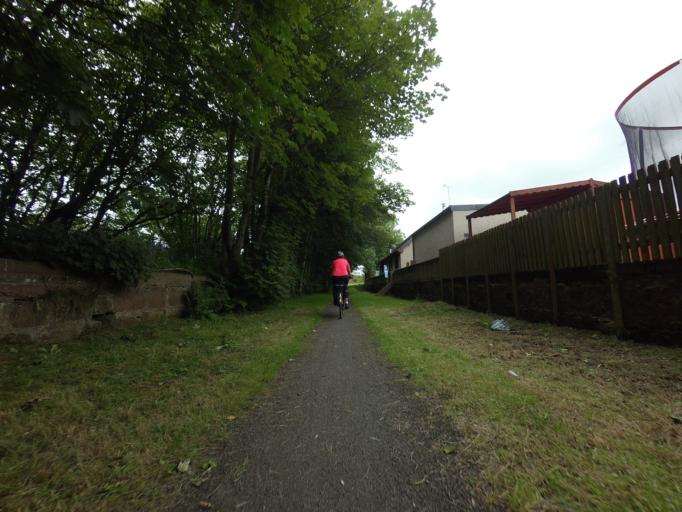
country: GB
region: Scotland
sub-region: Aberdeenshire
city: Ellon
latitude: 57.4667
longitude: -2.1170
